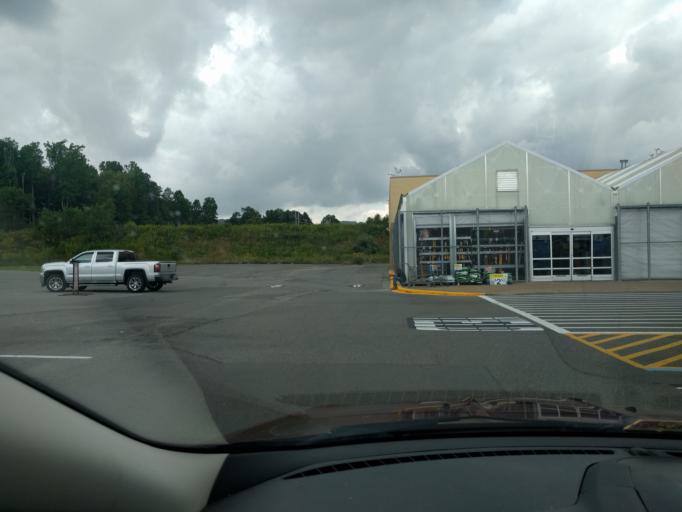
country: US
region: West Virginia
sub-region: Nicholas County
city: Summersville
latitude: 38.3037
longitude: -80.8365
